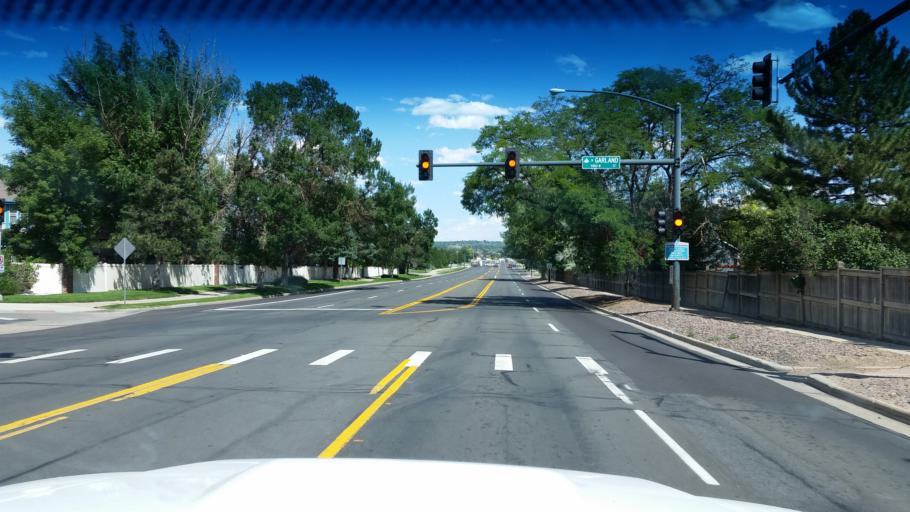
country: US
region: Colorado
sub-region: Broomfield County
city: Broomfield
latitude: 39.8781
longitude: -105.1031
